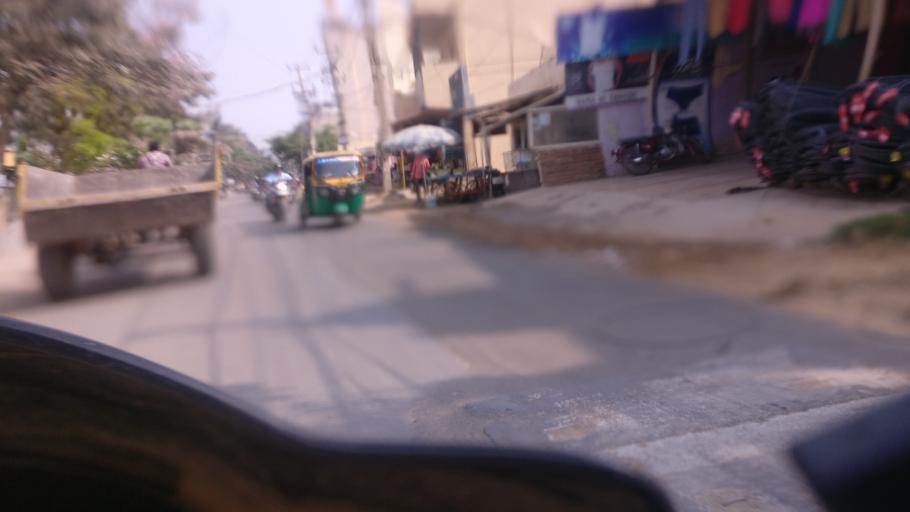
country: IN
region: Karnataka
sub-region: Bangalore Urban
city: Bangalore
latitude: 12.8827
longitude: 77.6723
